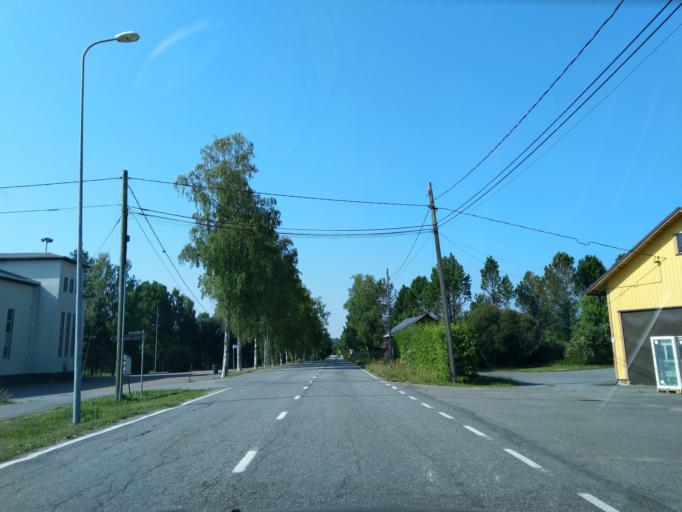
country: FI
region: Satakunta
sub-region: Pori
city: Pomarkku
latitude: 61.7011
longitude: 22.0187
